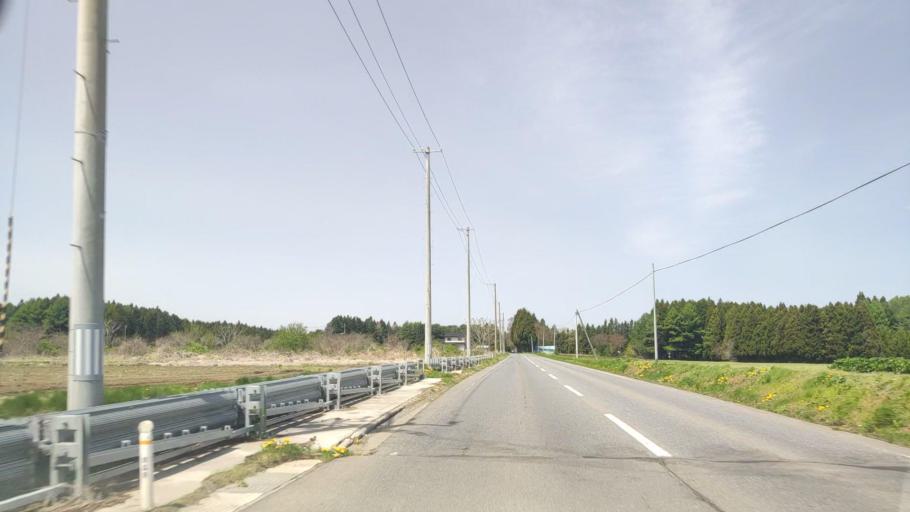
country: JP
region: Aomori
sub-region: Hachinohe Shi
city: Uchimaru
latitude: 40.5298
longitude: 141.4064
